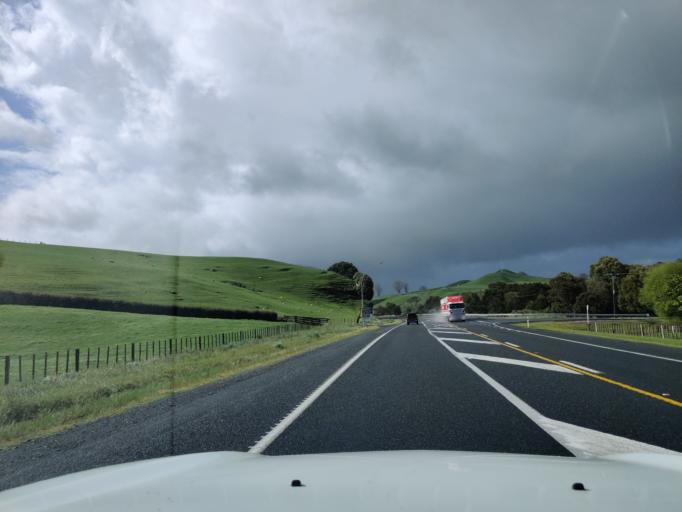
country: NZ
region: Waikato
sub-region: Matamata-Piako District
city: Matamata
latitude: -37.9496
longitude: 175.6742
